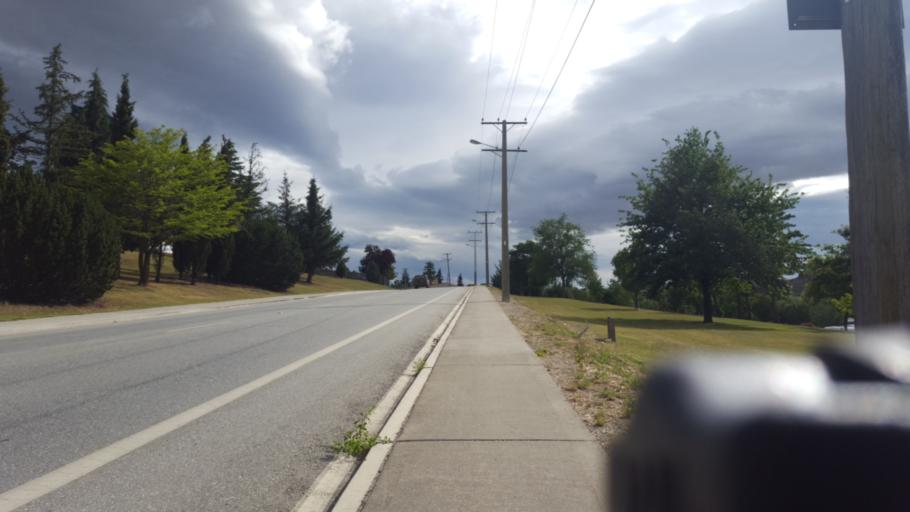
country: NZ
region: Otago
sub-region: Queenstown-Lakes District
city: Wanaka
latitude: -45.2478
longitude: 169.4006
